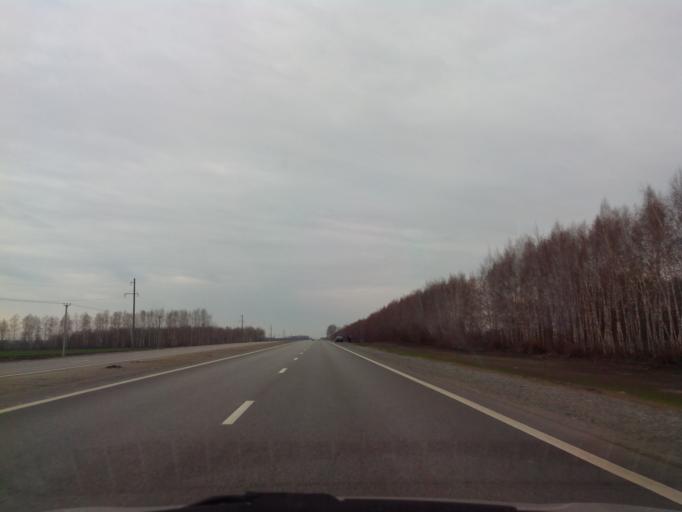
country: RU
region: Tambov
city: Zavoronezhskoye
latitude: 52.8803
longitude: 40.7374
